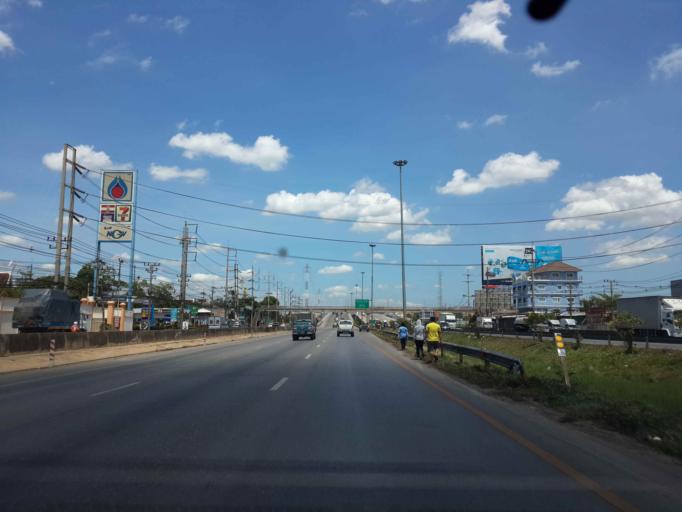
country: TH
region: Samut Sakhon
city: Samut Sakhon
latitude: 13.5433
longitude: 100.2439
